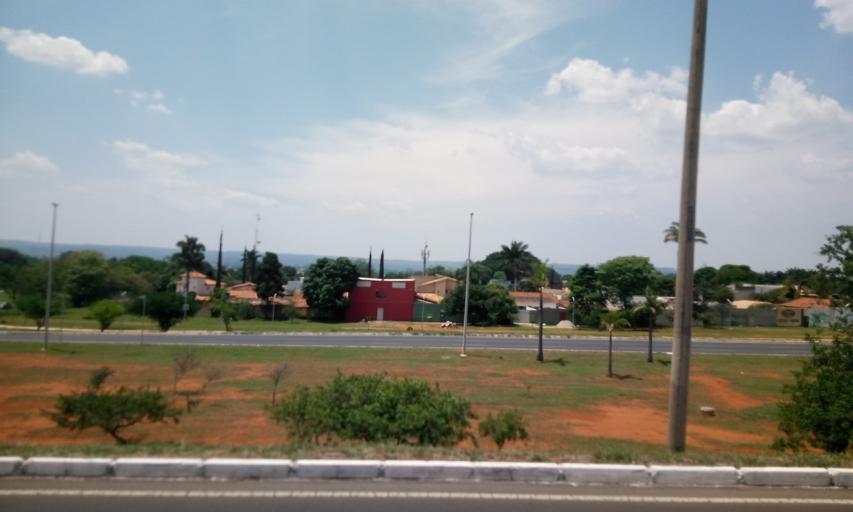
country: BR
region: Federal District
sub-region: Brasilia
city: Brasilia
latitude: -15.7935
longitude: -47.8591
